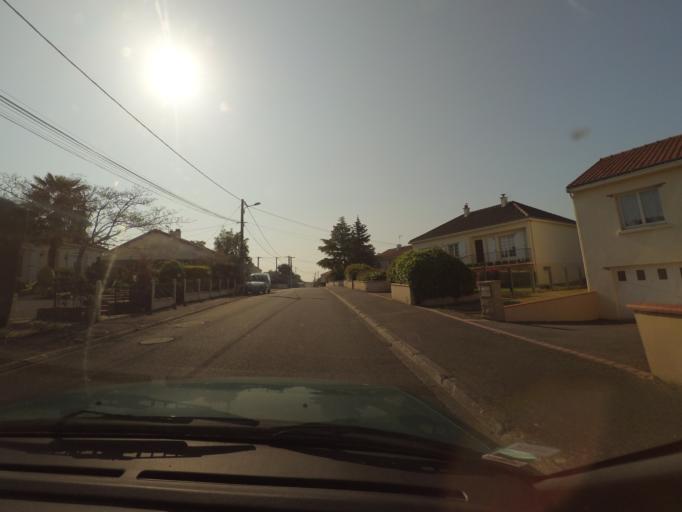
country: FR
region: Pays de la Loire
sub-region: Departement de la Loire-Atlantique
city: Mouzillon
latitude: 47.1432
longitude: -1.2865
